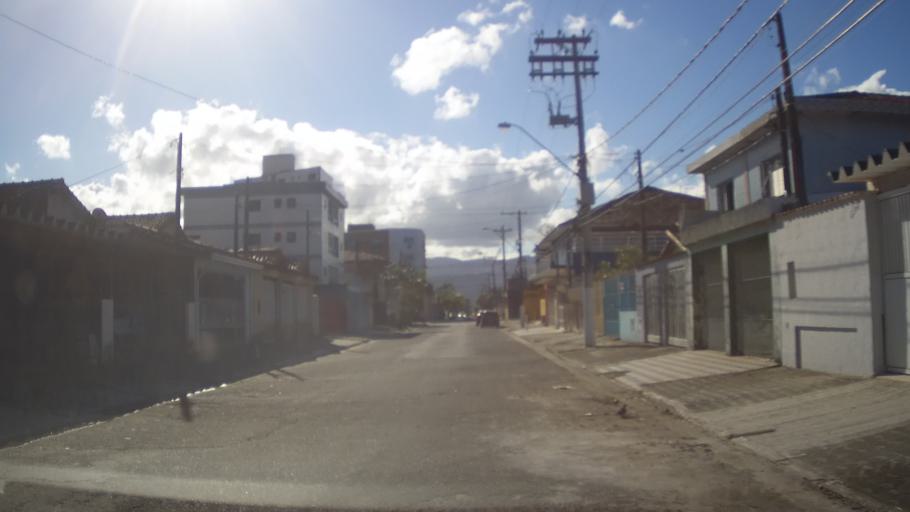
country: BR
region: Sao Paulo
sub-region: Praia Grande
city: Praia Grande
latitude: -24.0296
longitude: -46.4867
